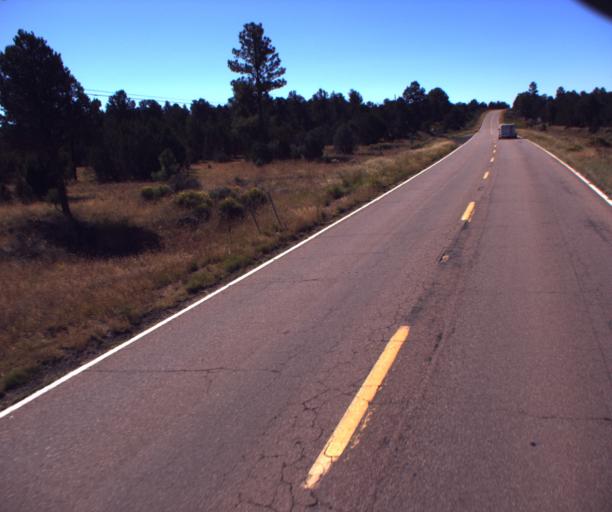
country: US
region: Arizona
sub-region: Navajo County
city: Heber-Overgaard
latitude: 34.4448
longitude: -110.5305
